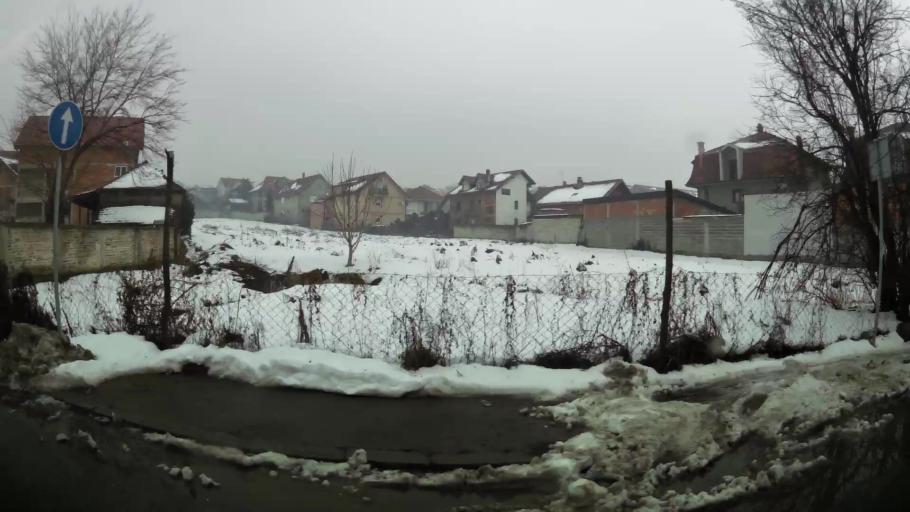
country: RS
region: Central Serbia
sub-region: Belgrade
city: Zvezdara
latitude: 44.7763
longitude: 20.5239
